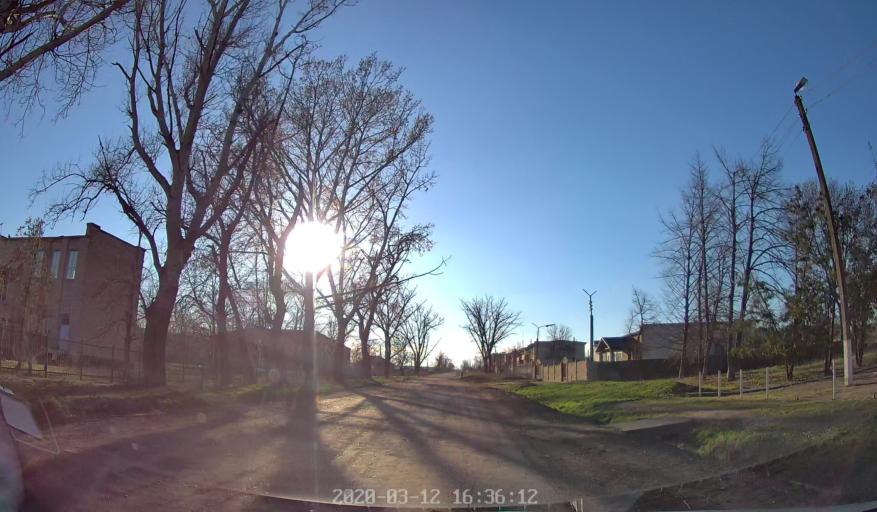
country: MD
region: Anenii Noi
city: Anenii Noi
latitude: 46.8156
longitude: 29.1995
